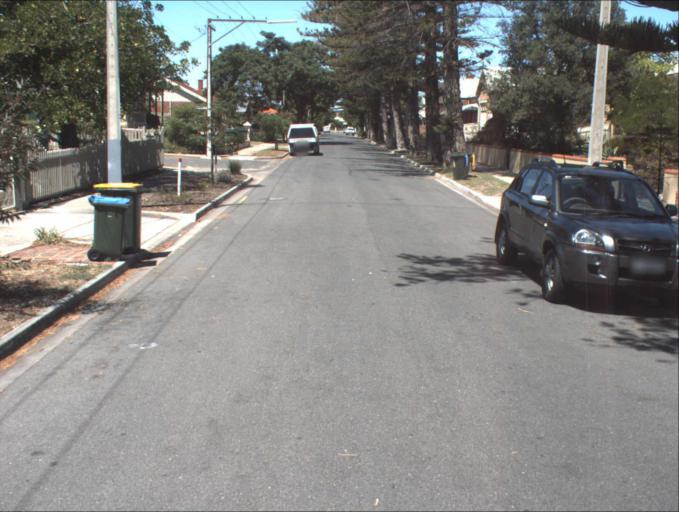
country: AU
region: South Australia
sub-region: Port Adelaide Enfield
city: Birkenhead
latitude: -34.8324
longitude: 138.4832
